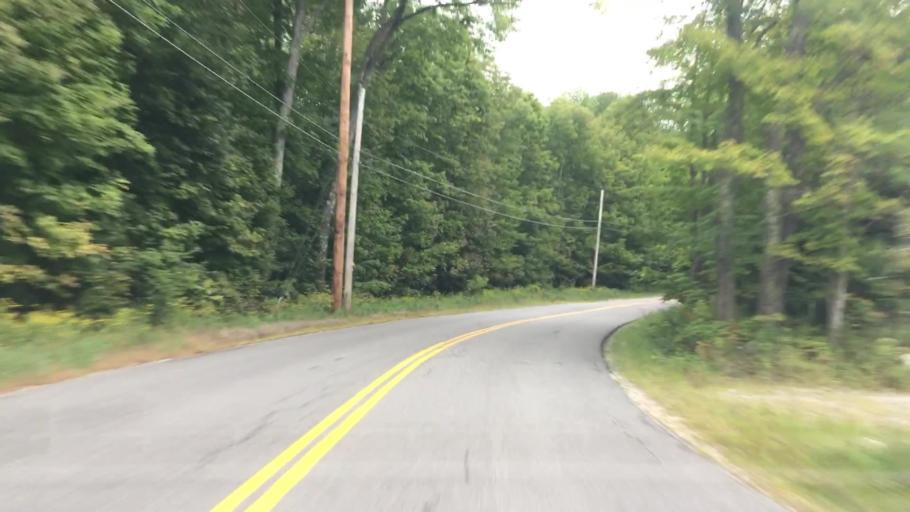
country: US
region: Maine
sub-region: Cumberland County
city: New Gloucester
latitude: 43.9066
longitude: -70.2193
